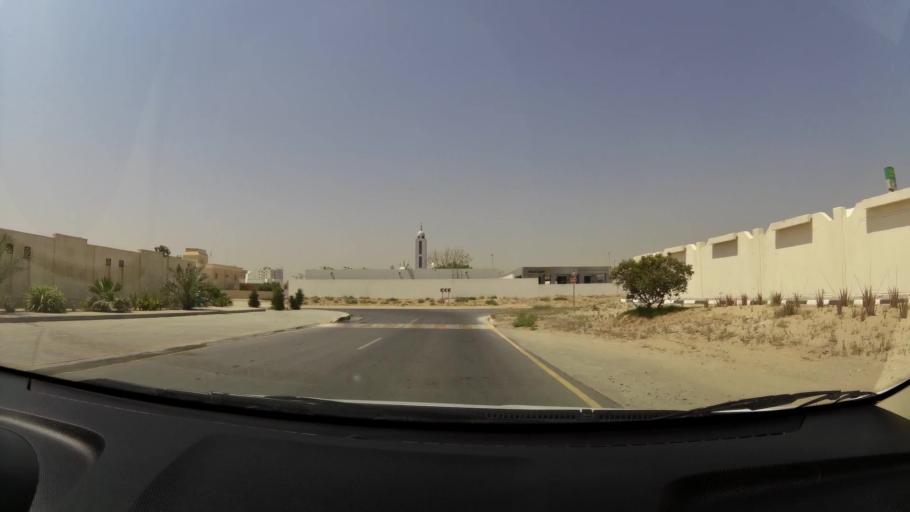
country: AE
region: Ajman
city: Ajman
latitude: 25.4147
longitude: 55.5140
